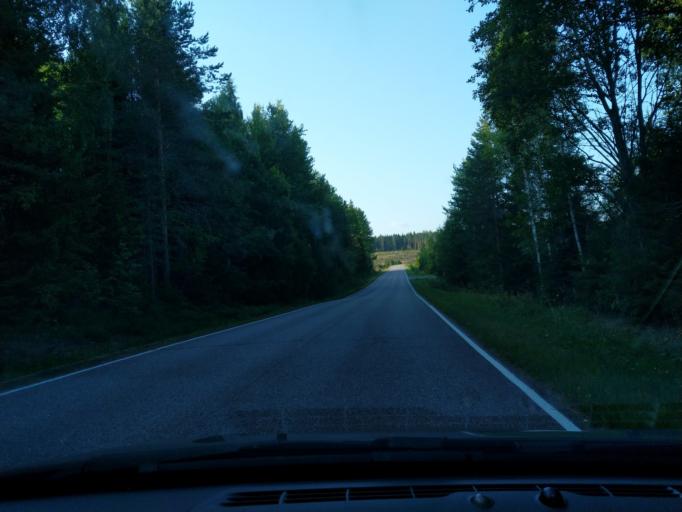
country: FI
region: Uusimaa
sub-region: Helsinki
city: Vihti
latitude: 60.5374
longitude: 24.3397
